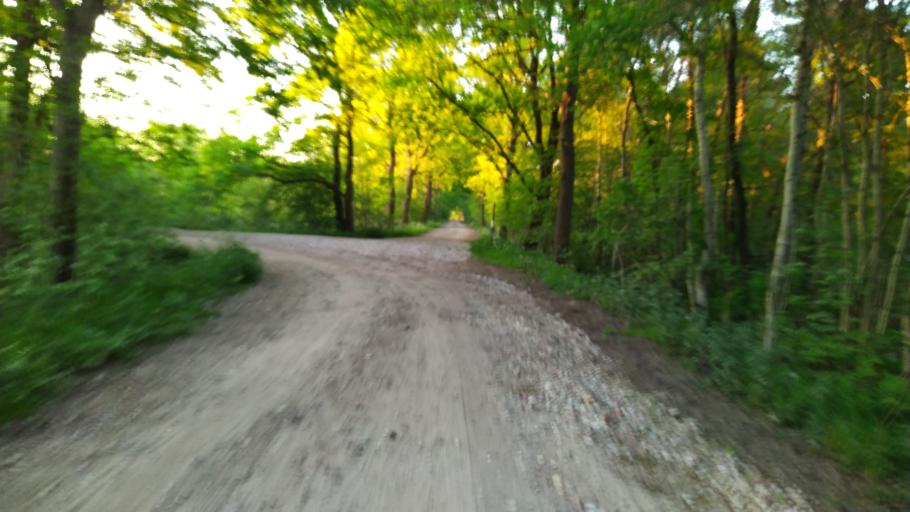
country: DE
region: Lower Saxony
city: Bargstedt
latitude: 53.4852
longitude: 9.4399
